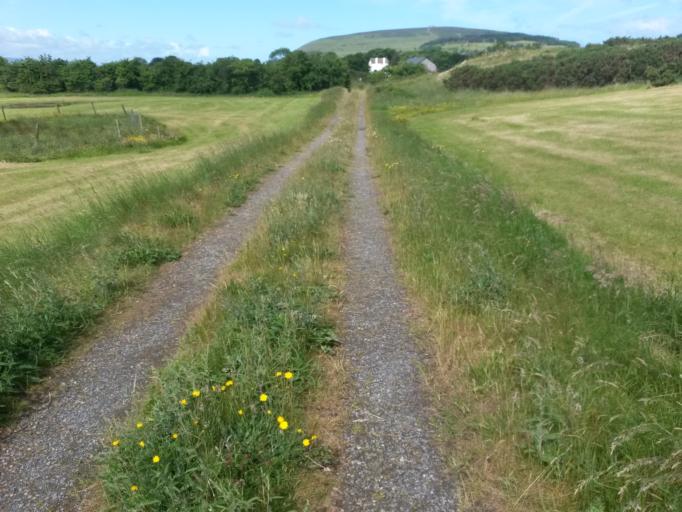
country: IE
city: Ballisodare
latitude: 54.2482
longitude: -8.5205
